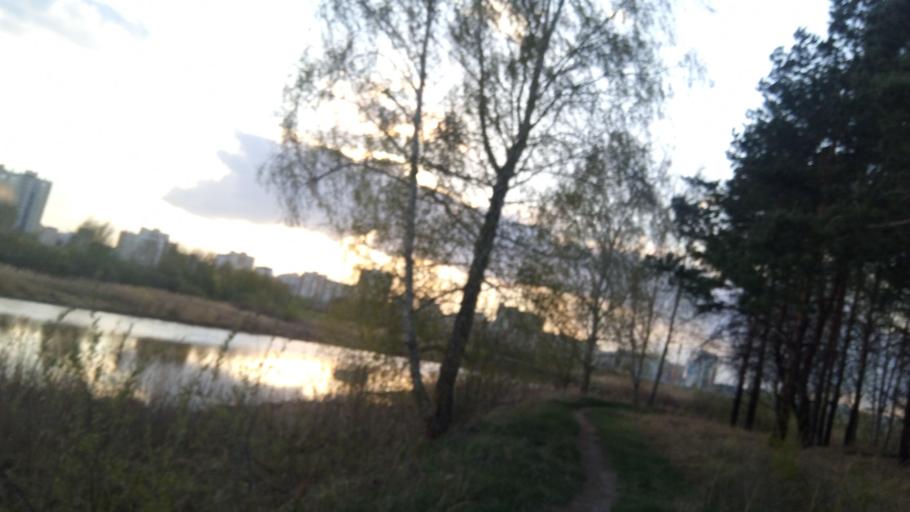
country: RU
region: Chelyabinsk
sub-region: Gorod Chelyabinsk
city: Chelyabinsk
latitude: 55.1607
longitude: 61.3141
